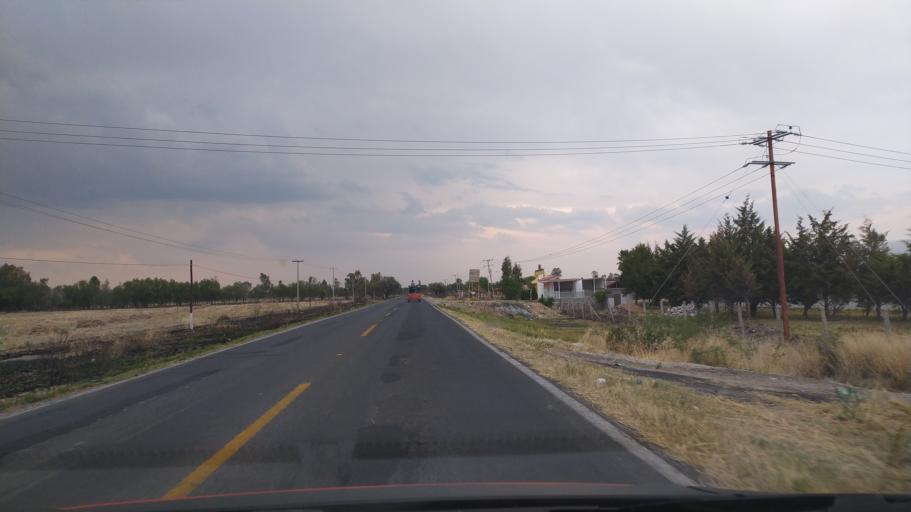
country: MX
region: Guanajuato
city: Ciudad Manuel Doblado
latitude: 20.7814
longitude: -101.9095
